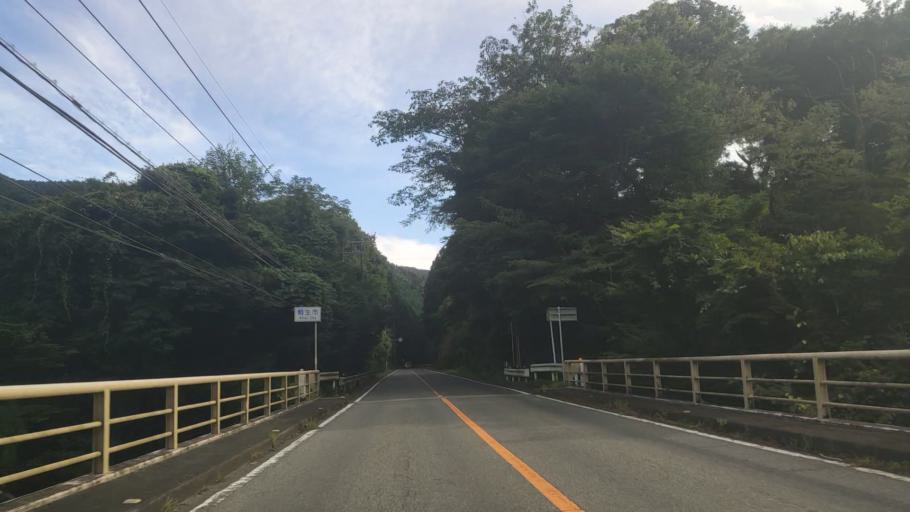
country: JP
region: Gunma
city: Omamacho-omama
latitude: 36.5078
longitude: 139.2957
